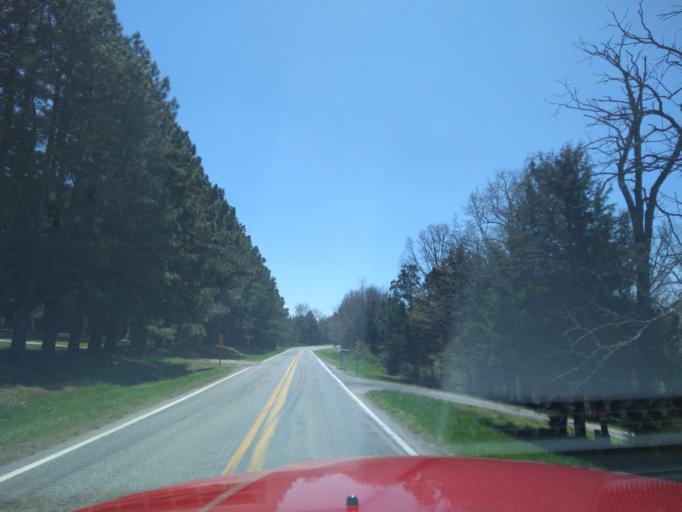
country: US
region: Arkansas
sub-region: Washington County
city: West Fork
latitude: 35.8340
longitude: -94.2677
